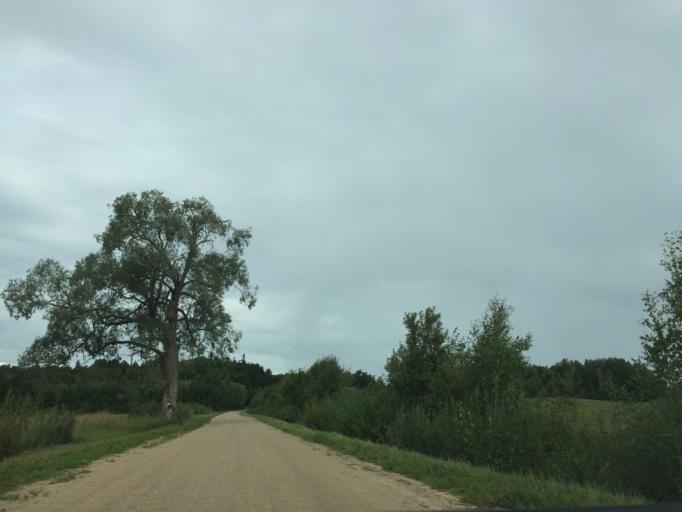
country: LV
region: Pargaujas
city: Stalbe
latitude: 57.5175
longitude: 24.9163
